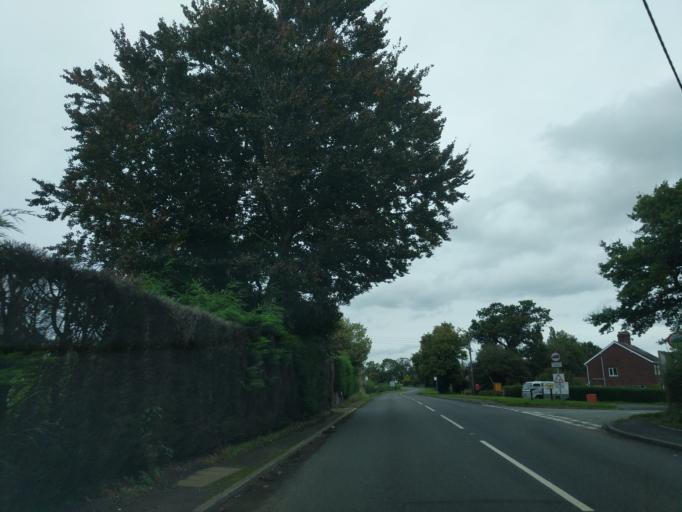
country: GB
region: England
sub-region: Cheshire East
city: Chorlton
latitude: 53.0490
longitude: -2.3798
